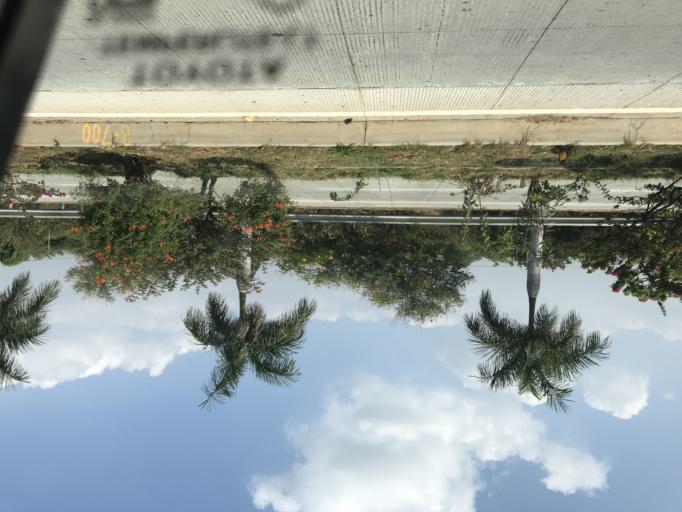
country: IN
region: Karnataka
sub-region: Bangalore Urban
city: Bangalore
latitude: 12.8847
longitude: 77.5028
